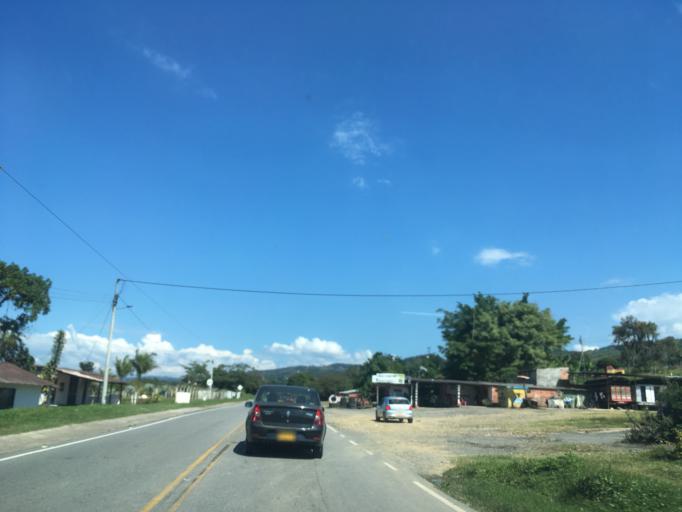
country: CO
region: Santander
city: Suaita
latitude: 6.0751
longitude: -73.4053
